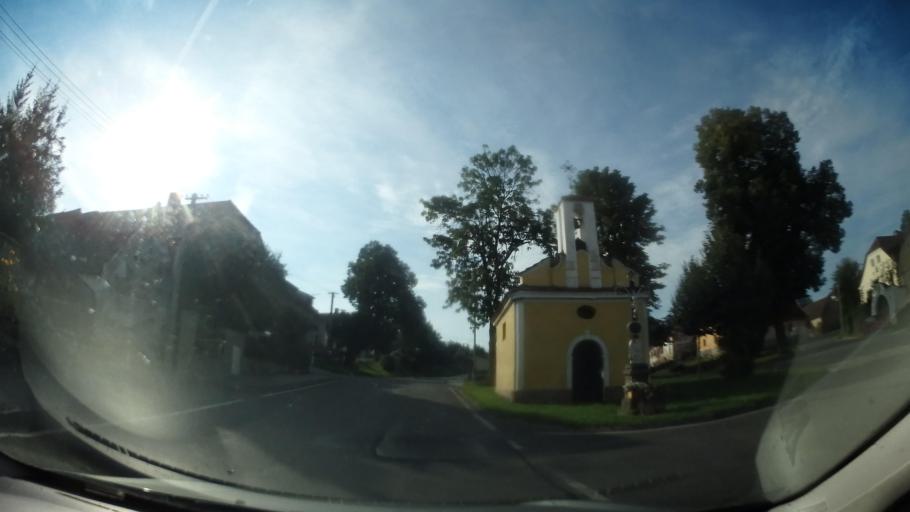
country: CZ
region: Jihocesky
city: Cimelice
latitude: 49.4180
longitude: 14.1168
